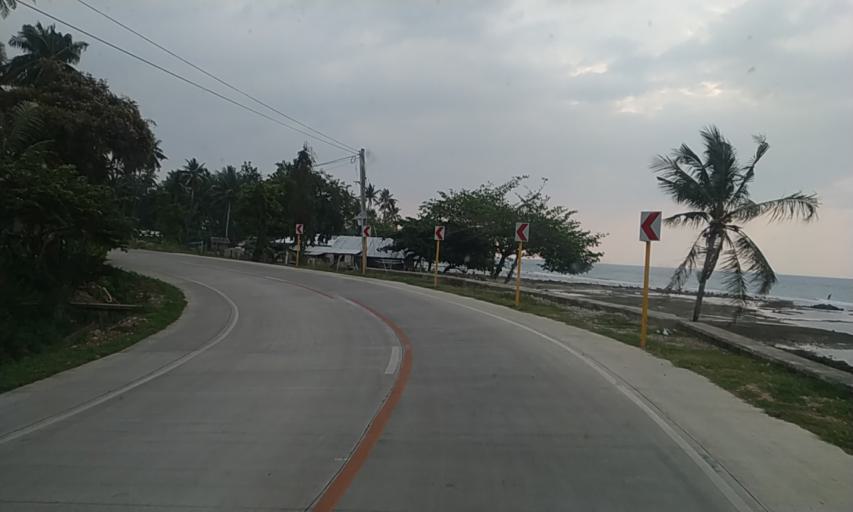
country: PH
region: Central Visayas
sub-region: Province of Negros Oriental
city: Calamba
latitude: 10.1905
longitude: 123.2937
